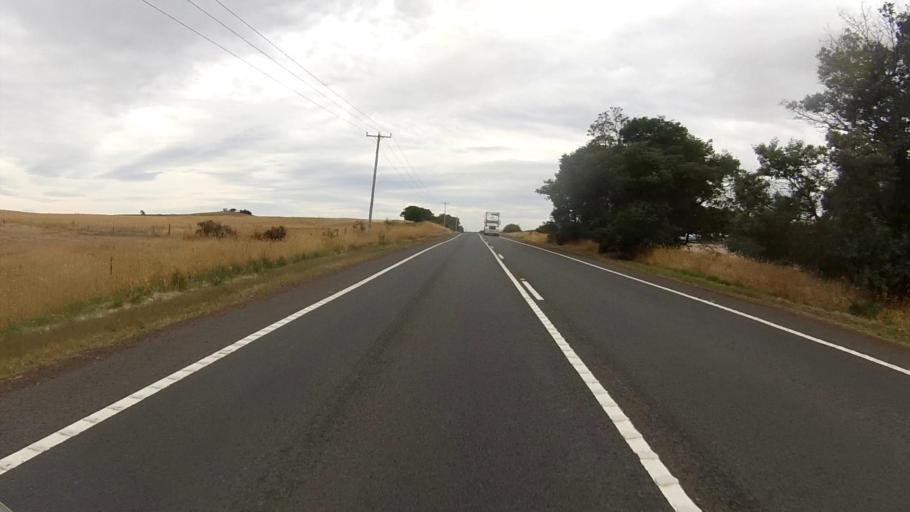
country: AU
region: Tasmania
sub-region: Northern Midlands
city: Evandale
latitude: -41.9076
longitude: 147.4799
